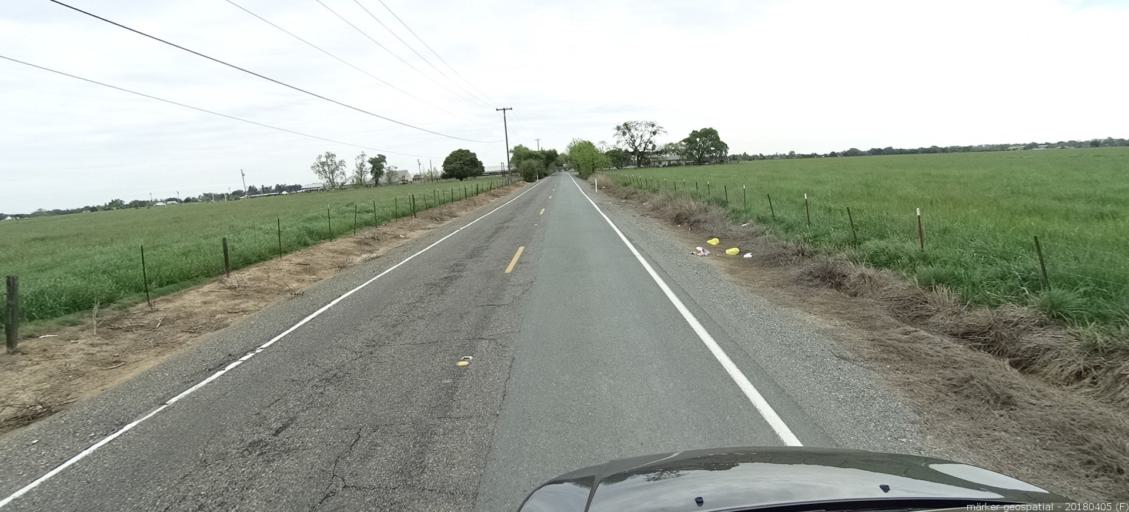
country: US
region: California
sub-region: Sacramento County
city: Galt
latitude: 38.2473
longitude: -121.3507
